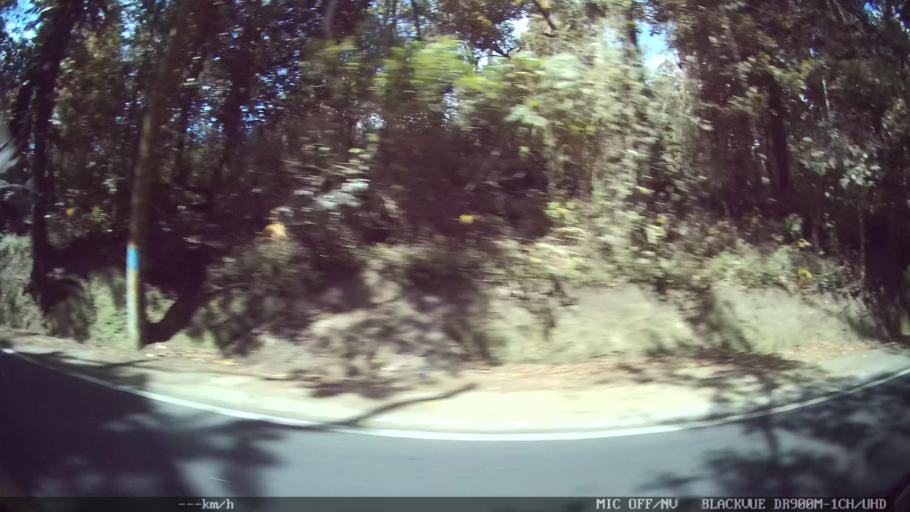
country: ID
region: Bali
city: Banjar Kedisan
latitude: -8.2884
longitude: 115.3739
